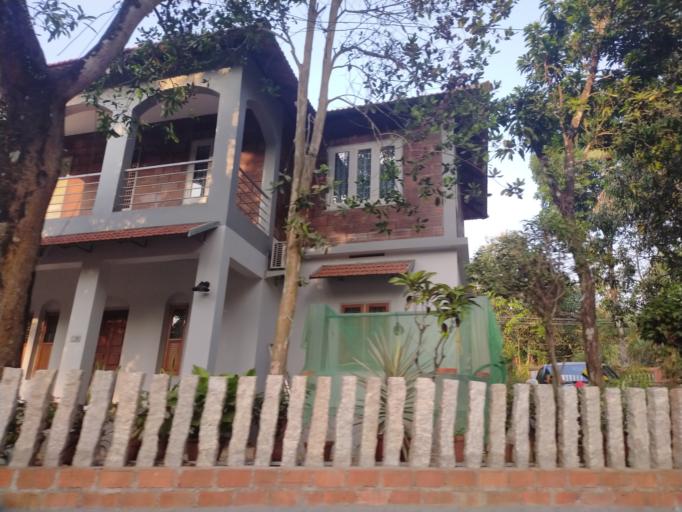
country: IN
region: Kerala
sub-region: Kottayam
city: Palackattumala
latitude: 9.7465
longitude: 76.5128
